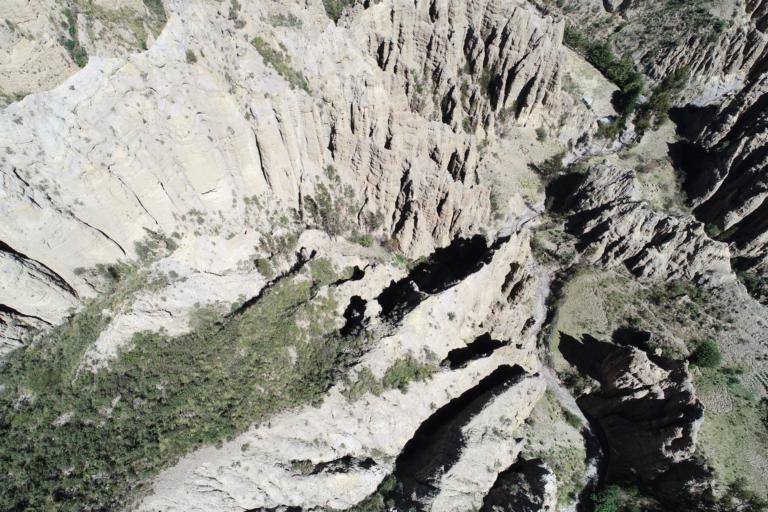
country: BO
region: La Paz
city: La Paz
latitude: -16.5041
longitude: -68.0640
